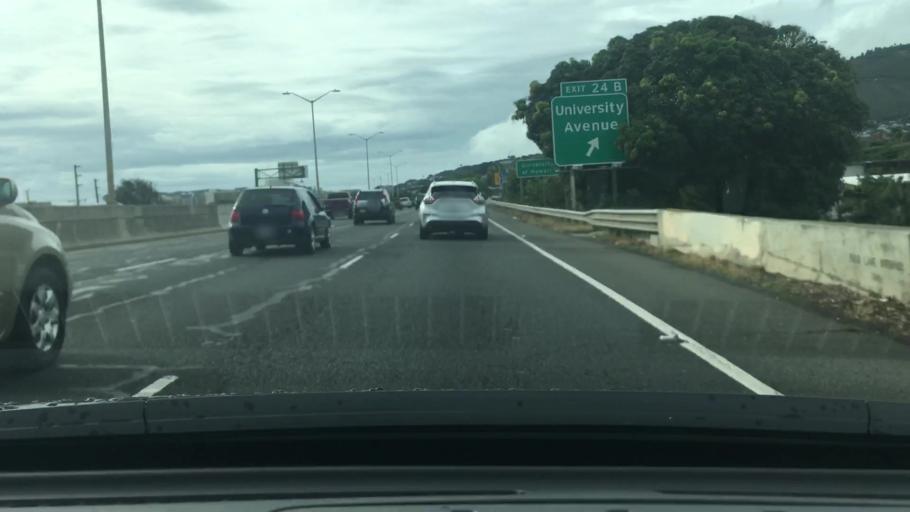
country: US
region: Hawaii
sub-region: Honolulu County
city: Honolulu
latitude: 21.2924
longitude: -157.8192
